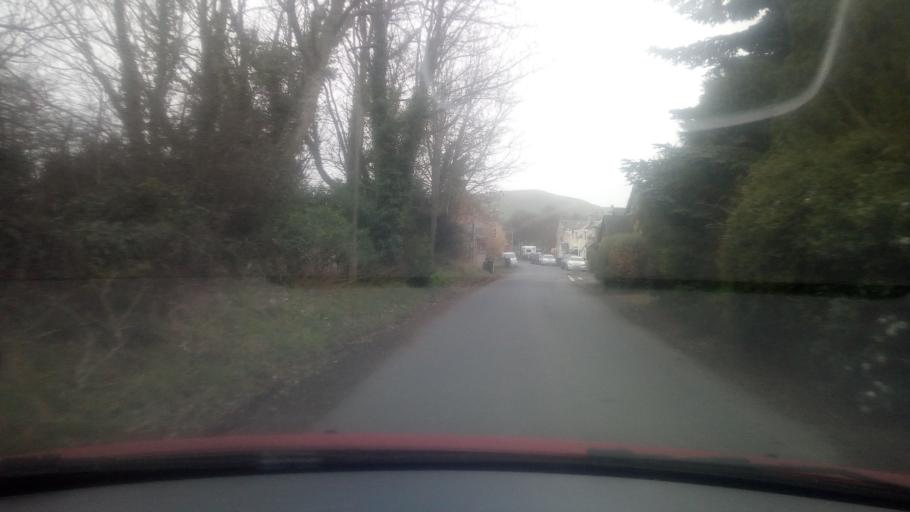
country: GB
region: Scotland
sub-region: The Scottish Borders
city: Hawick
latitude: 55.4560
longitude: -2.6842
